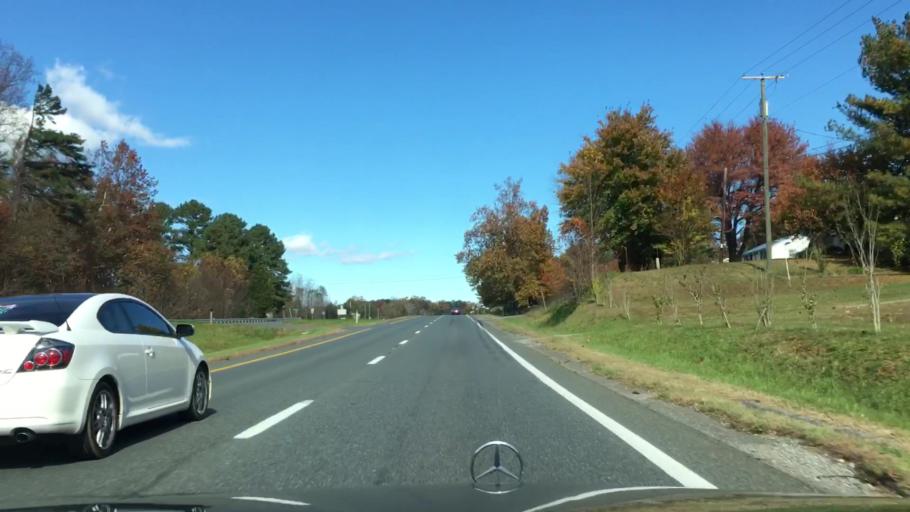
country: US
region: Virginia
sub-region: Campbell County
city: Altavista
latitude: 37.1961
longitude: -79.2035
